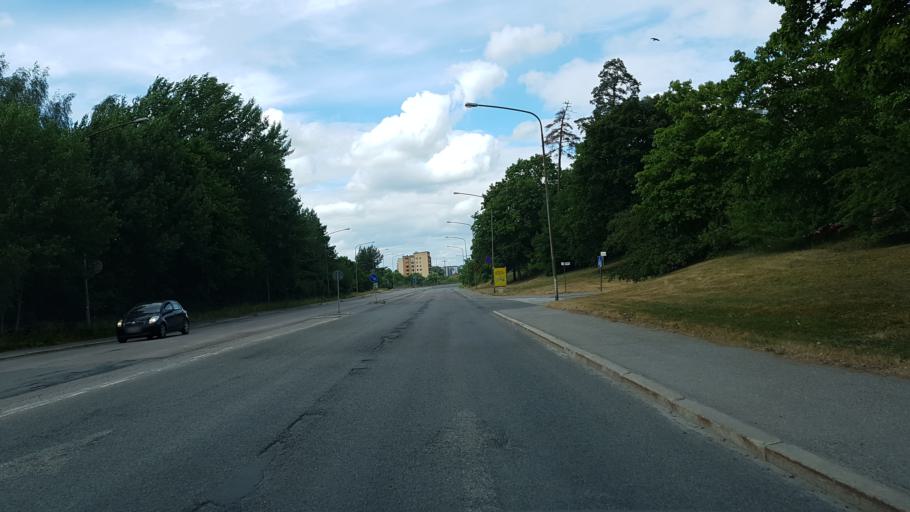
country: SE
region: Stockholm
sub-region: Solna Kommun
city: Solna
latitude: 59.3511
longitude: 17.9898
